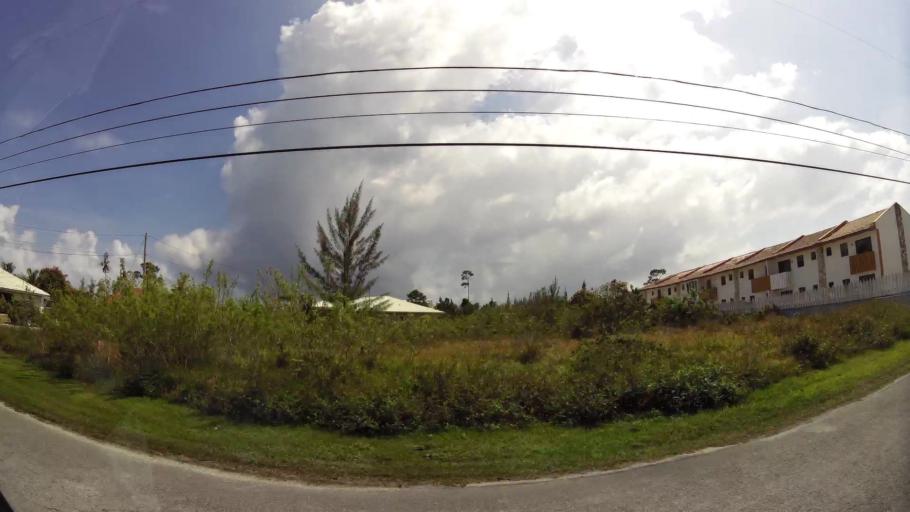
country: BS
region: Freeport
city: Freeport
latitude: 26.4994
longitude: -78.7056
